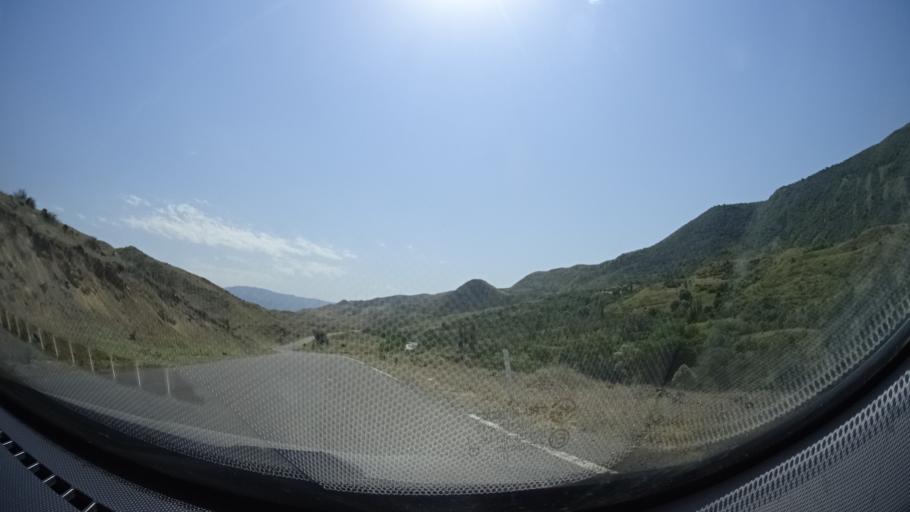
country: GE
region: Samtskhe-Javakheti
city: Aspindza
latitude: 41.5939
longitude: 43.1654
